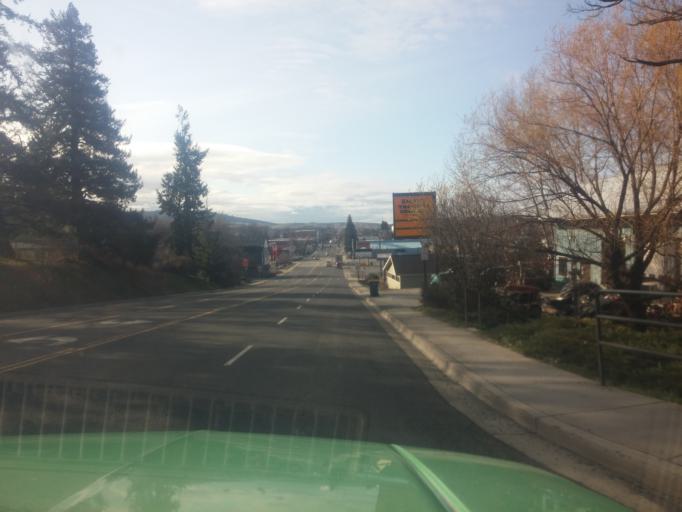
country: US
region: Idaho
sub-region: Latah County
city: Moscow
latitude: 46.7397
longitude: -117.0016
